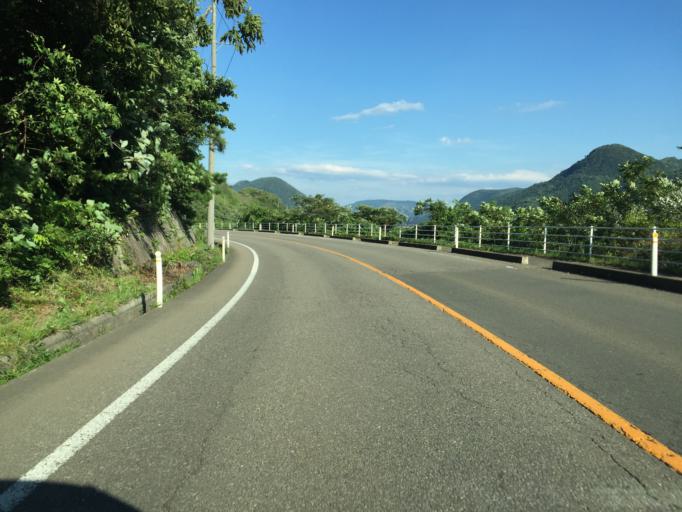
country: JP
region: Miyagi
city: Shiroishi
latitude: 37.9822
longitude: 140.4767
